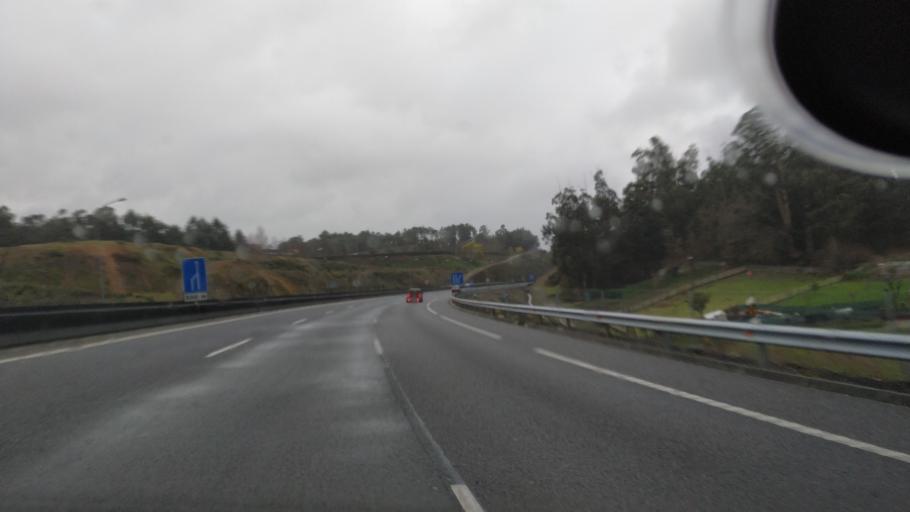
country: ES
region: Galicia
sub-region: Provincia da Coruna
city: Santiago de Compostela
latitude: 42.8470
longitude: -8.5329
